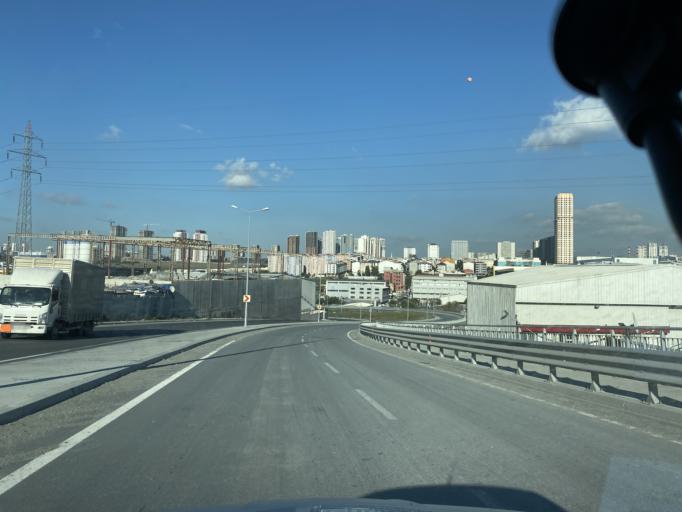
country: TR
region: Istanbul
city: Esenyurt
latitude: 41.0573
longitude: 28.6496
